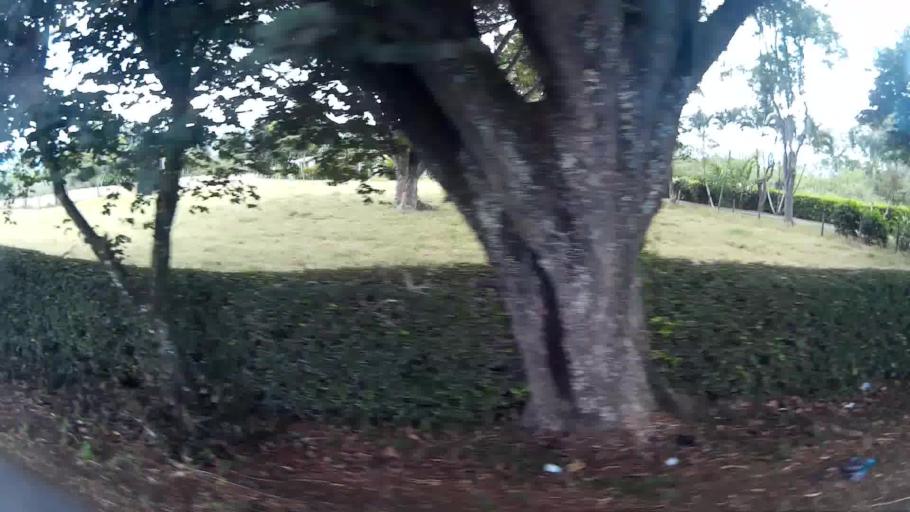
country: CO
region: Risaralda
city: La Virginia
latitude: 4.9110
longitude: -75.8714
